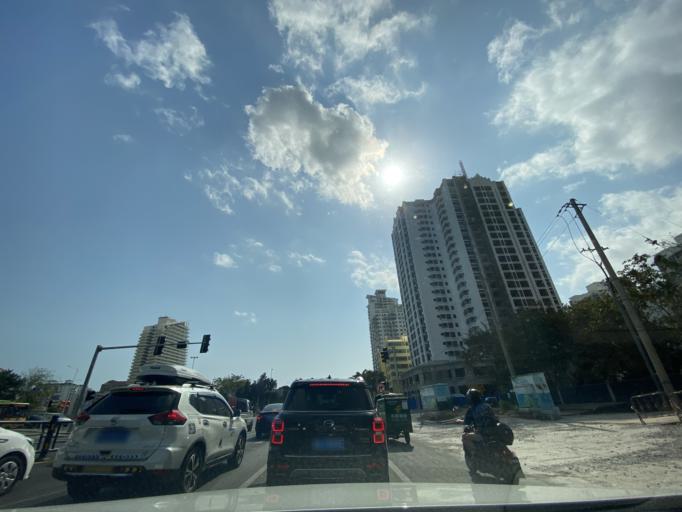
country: CN
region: Hainan
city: Sanya
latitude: 18.2640
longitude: 109.4936
